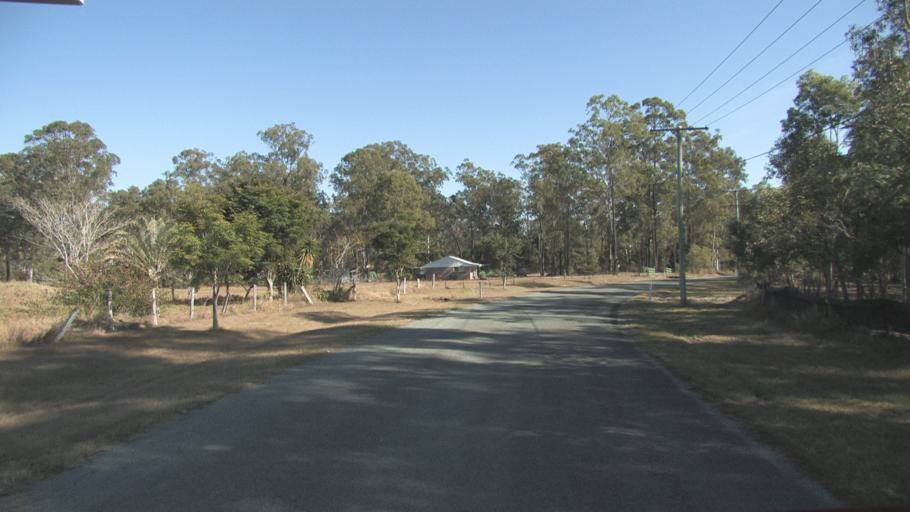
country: AU
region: Queensland
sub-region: Logan
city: Cedar Vale
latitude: -27.8317
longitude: 153.0443
